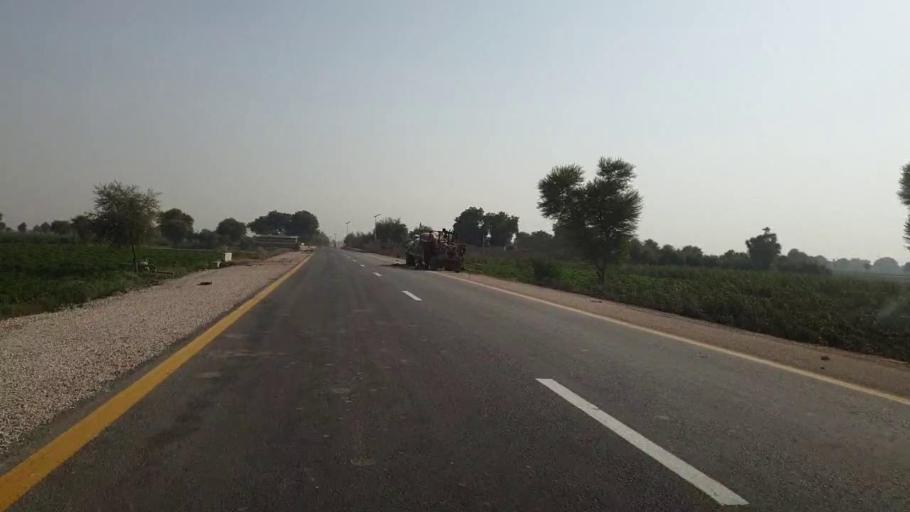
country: PK
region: Sindh
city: Bhan
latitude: 26.5373
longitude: 67.7881
